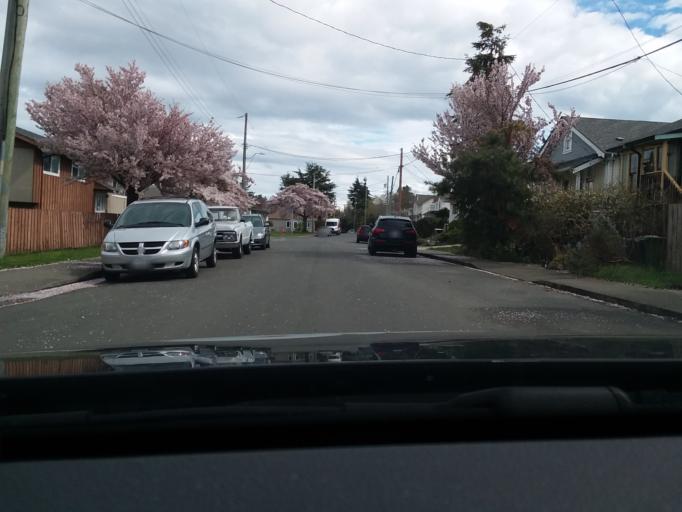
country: CA
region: British Columbia
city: Victoria
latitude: 48.4339
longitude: -123.3487
